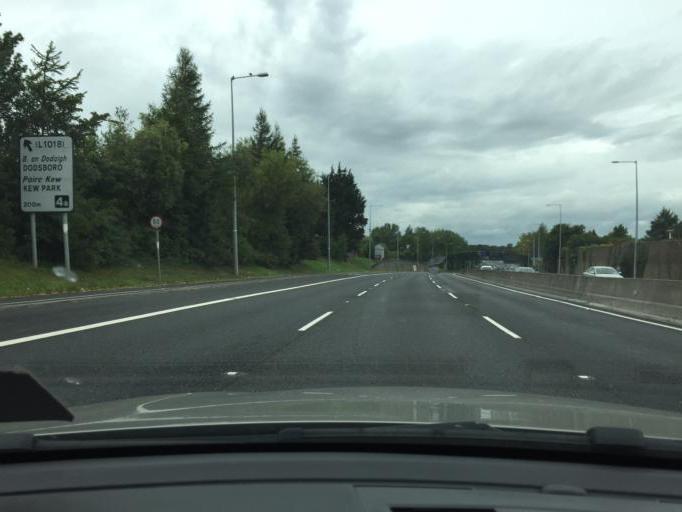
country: IE
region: Leinster
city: Lucan
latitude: 53.3525
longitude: -6.4560
